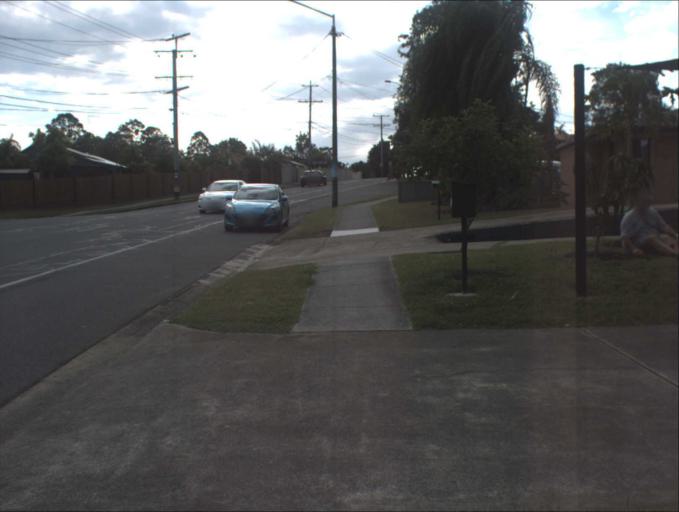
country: AU
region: Queensland
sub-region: Logan
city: Slacks Creek
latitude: -27.6426
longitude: 153.1650
